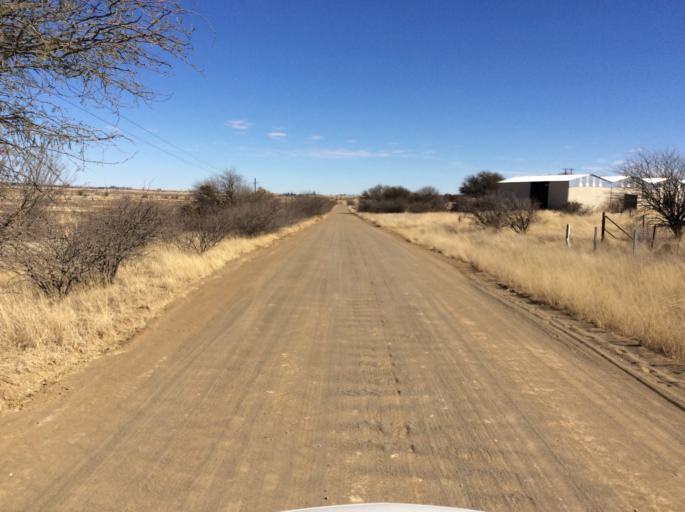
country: ZA
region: Orange Free State
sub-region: Lejweleputswa District Municipality
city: Brandfort
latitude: -28.7230
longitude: 26.0646
